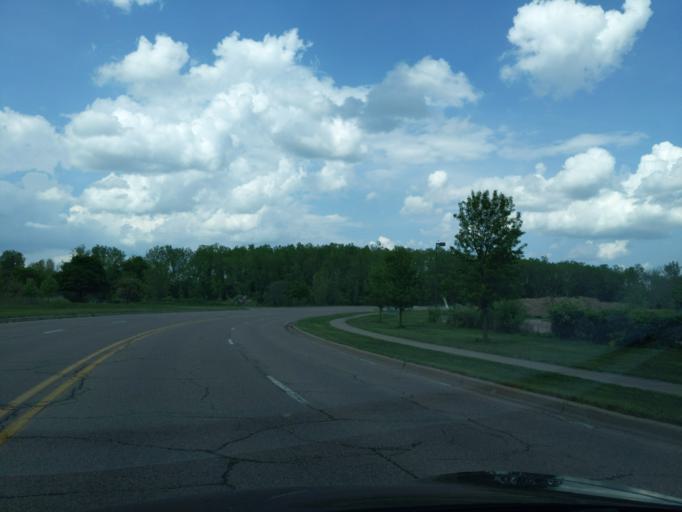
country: US
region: Michigan
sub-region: Ingham County
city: Okemos
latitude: 42.7279
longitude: -84.4222
